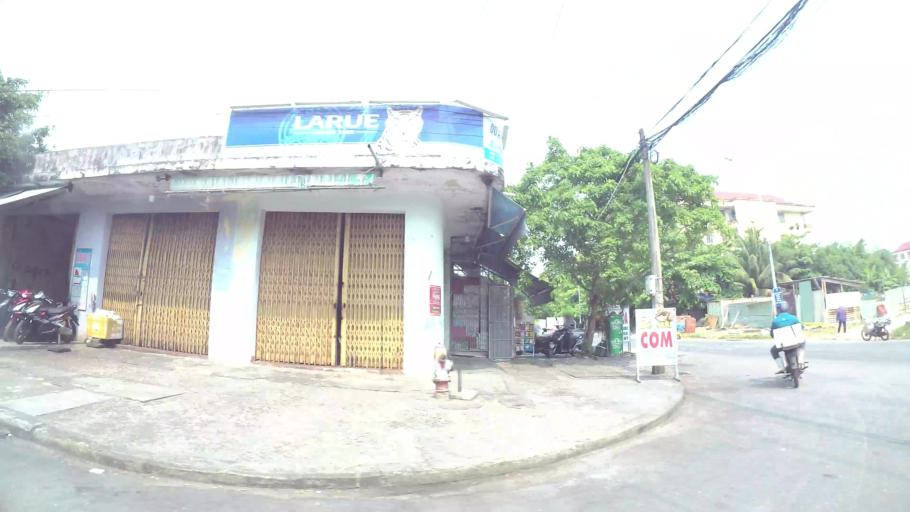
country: VN
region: Da Nang
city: Da Nang
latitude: 16.0891
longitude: 108.2367
